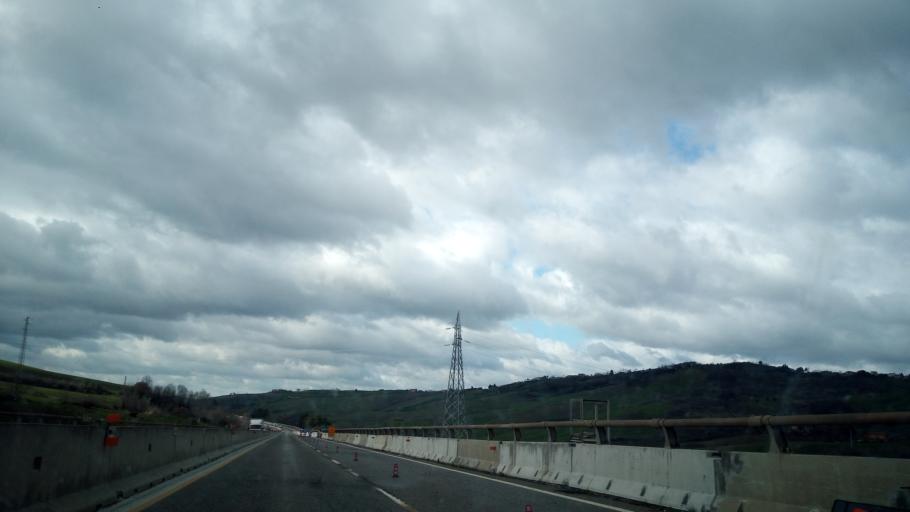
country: IT
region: Campania
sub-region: Provincia di Avellino
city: Flumeri
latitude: 41.0910
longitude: 15.1546
